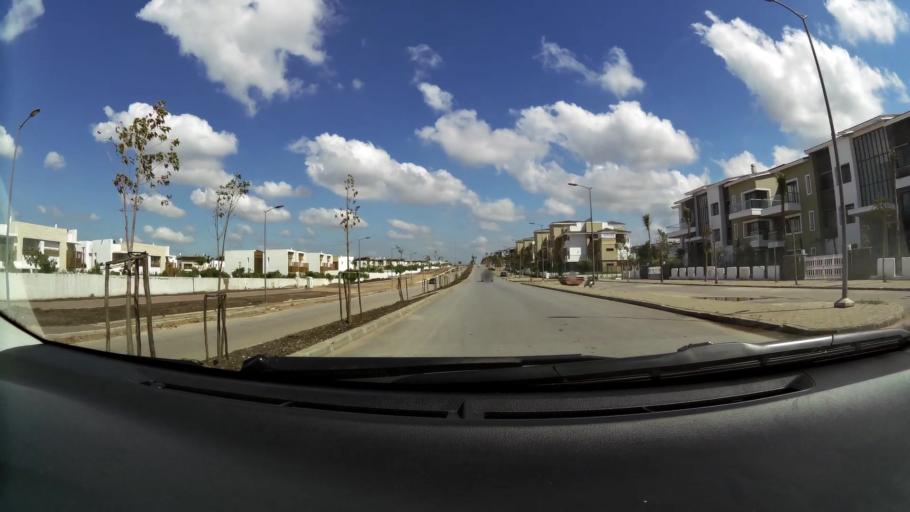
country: MA
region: Grand Casablanca
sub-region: Nouaceur
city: Bouskoura
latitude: 33.4852
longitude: -7.5973
